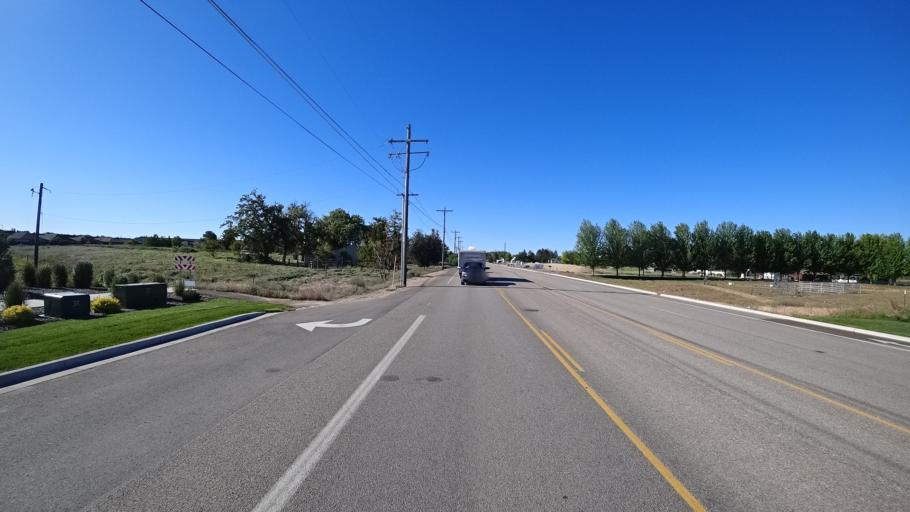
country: US
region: Idaho
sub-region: Ada County
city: Meridian
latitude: 43.6691
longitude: -116.4136
